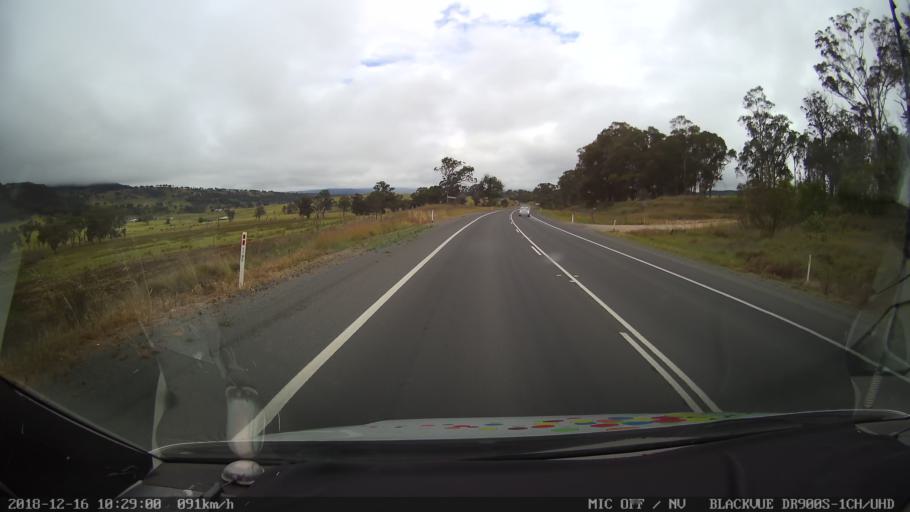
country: AU
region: New South Wales
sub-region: Tenterfield Municipality
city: Carrolls Creek
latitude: -29.1139
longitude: 151.9965
